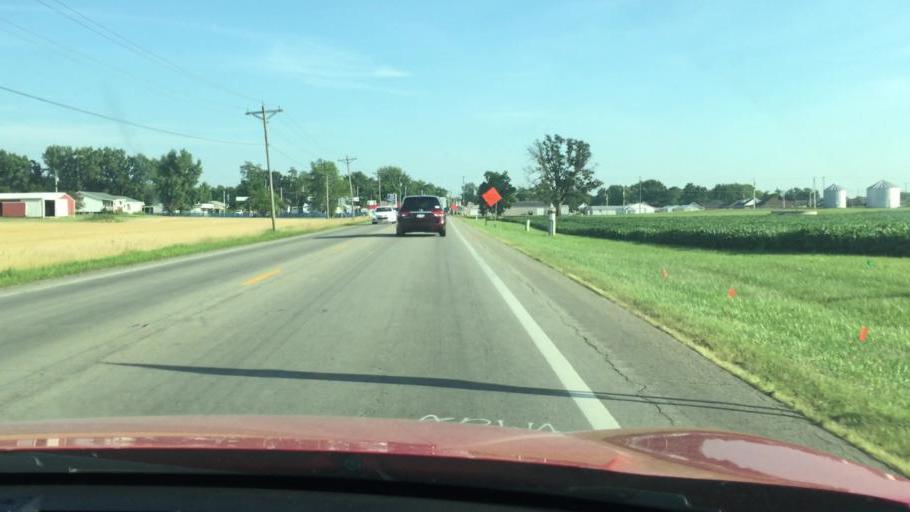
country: US
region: Ohio
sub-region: Logan County
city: Northwood
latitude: 40.4503
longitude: -83.8072
